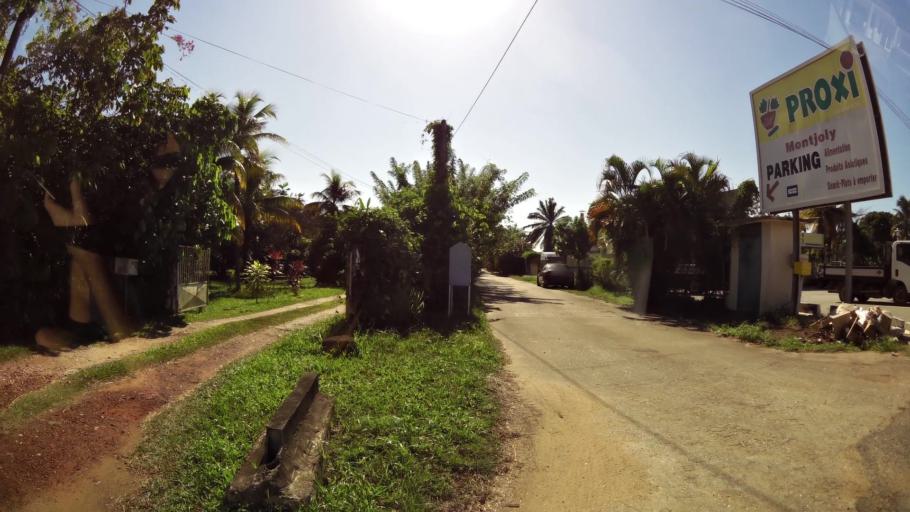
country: GF
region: Guyane
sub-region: Guyane
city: Remire-Montjoly
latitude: 4.9068
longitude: -52.2730
